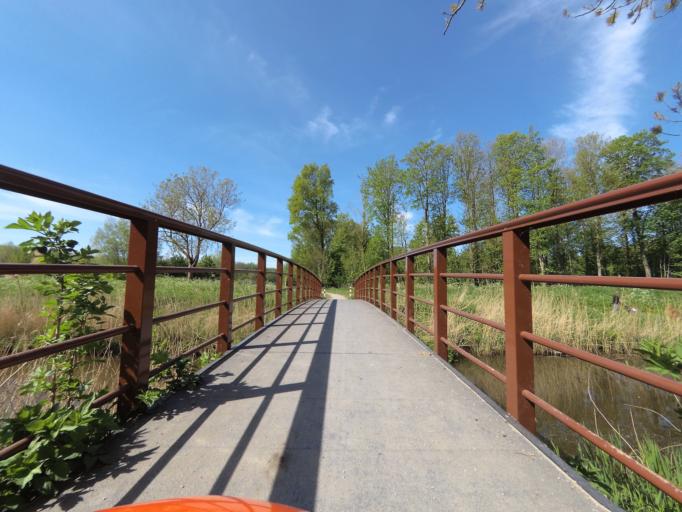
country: NL
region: Flevoland
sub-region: Gemeente Dronten
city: Dronten
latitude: 52.5228
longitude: 5.6829
